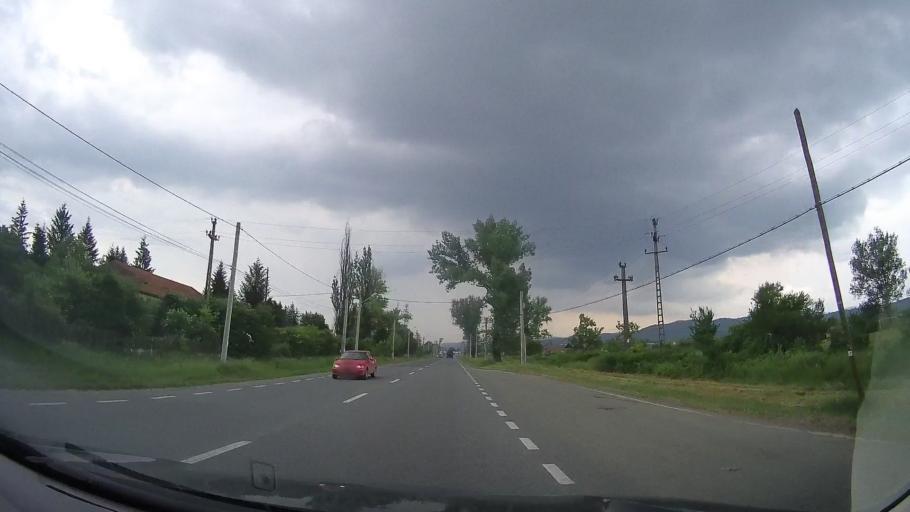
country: RO
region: Caras-Severin
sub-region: Municipiul Caransebes
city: Caransebes
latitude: 45.4328
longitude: 22.1948
